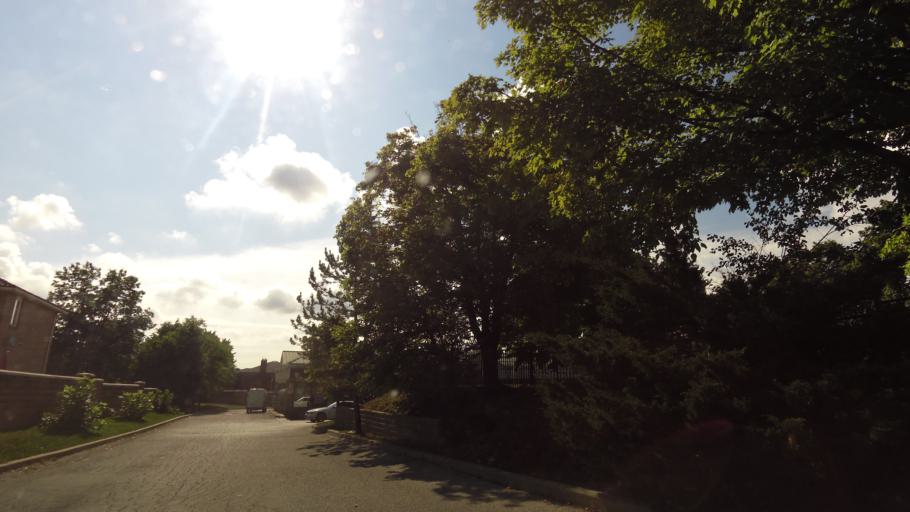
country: CA
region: Ontario
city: Brampton
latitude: 43.7264
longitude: -79.8133
